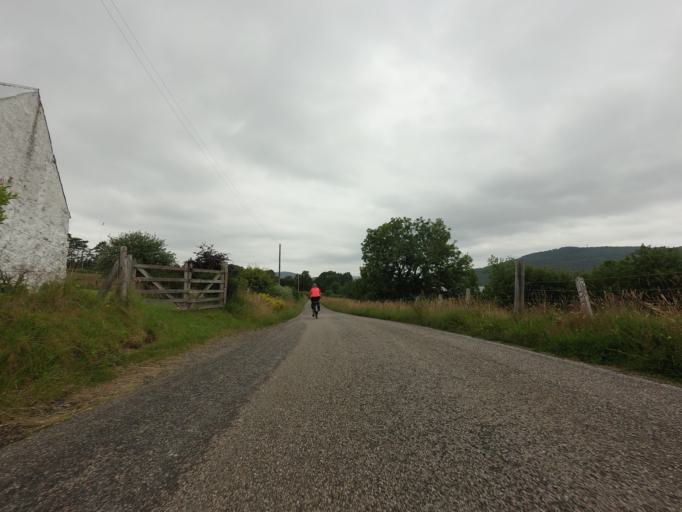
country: GB
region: Scotland
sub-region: Highland
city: Evanton
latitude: 57.9030
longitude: -4.3870
